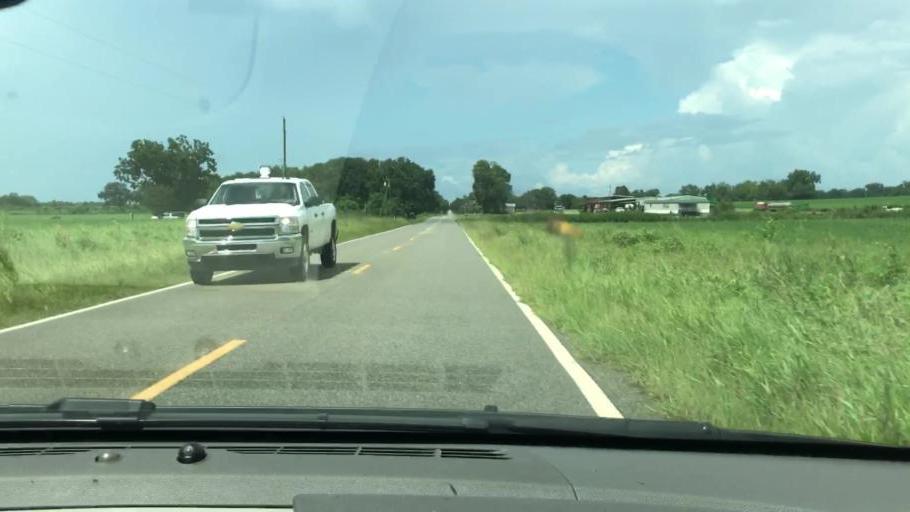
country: US
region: Georgia
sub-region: Seminole County
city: Donalsonville
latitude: 31.1139
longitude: -84.9958
